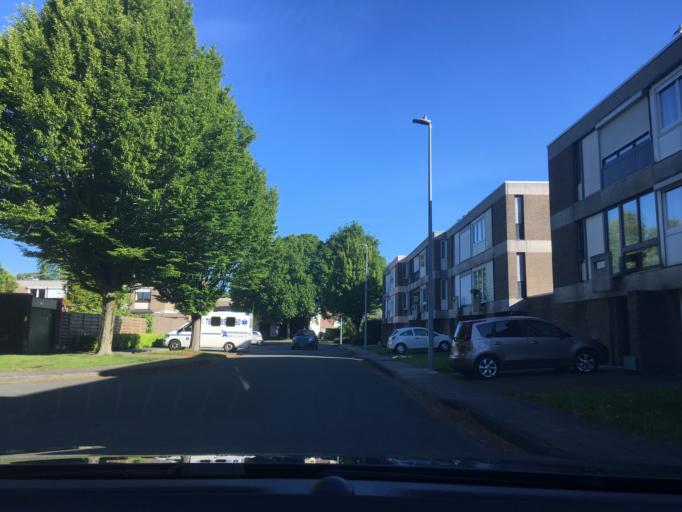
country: BE
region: Flanders
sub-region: Provincie West-Vlaanderen
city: Oostkamp
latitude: 51.1734
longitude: 3.2156
